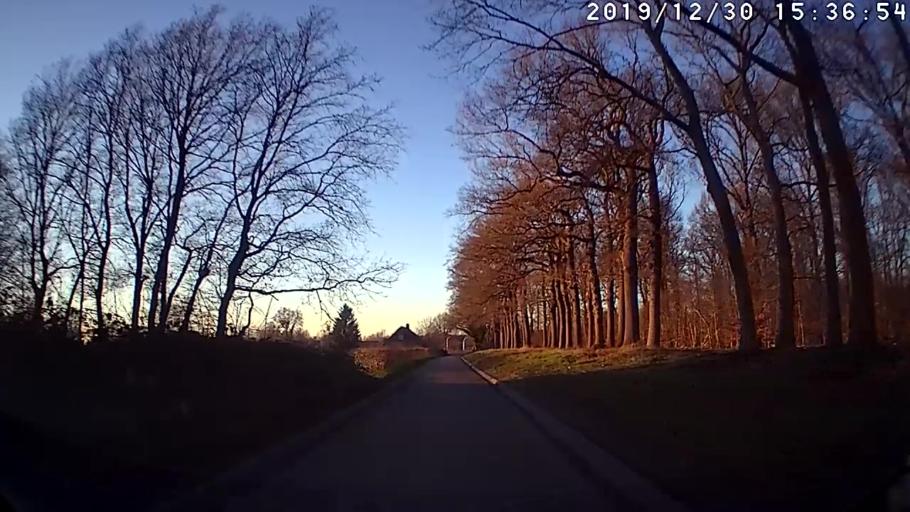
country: NL
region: Overijssel
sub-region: Gemeente Raalte
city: Heino
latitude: 52.4555
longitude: 6.1818
